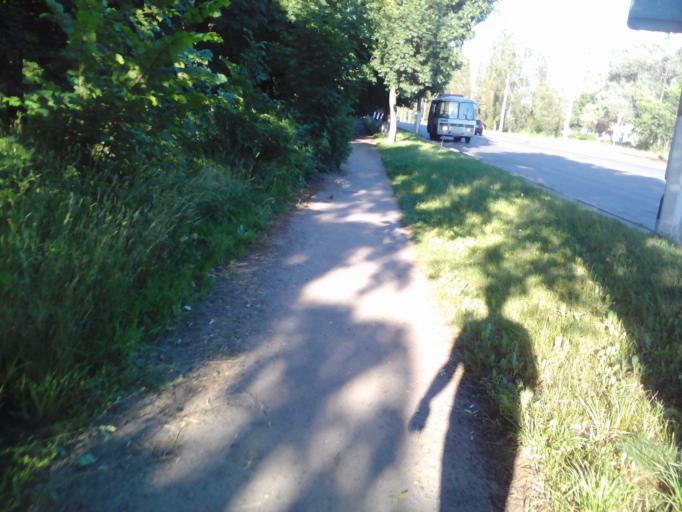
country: RU
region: Kursk
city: Voroshnevo
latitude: 51.6683
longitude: 36.0838
